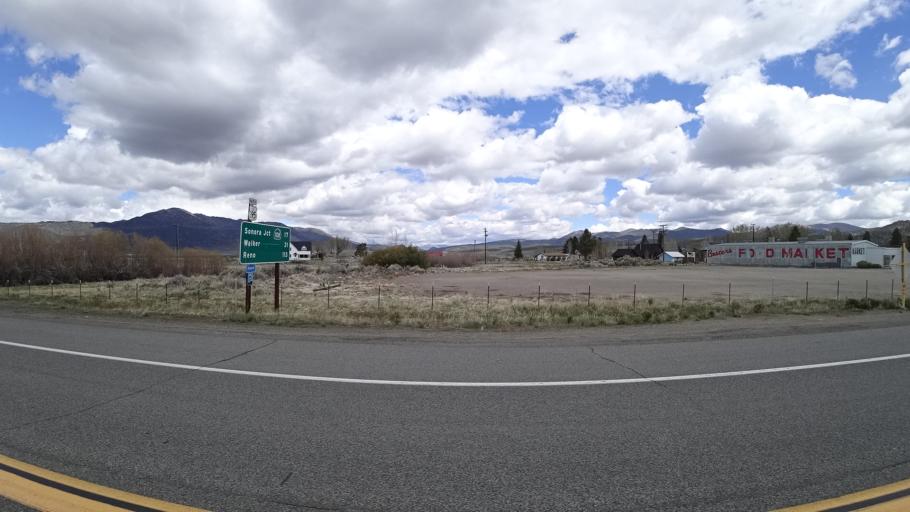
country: US
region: California
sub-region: Mono County
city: Bridgeport
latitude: 38.2563
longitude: -119.2333
